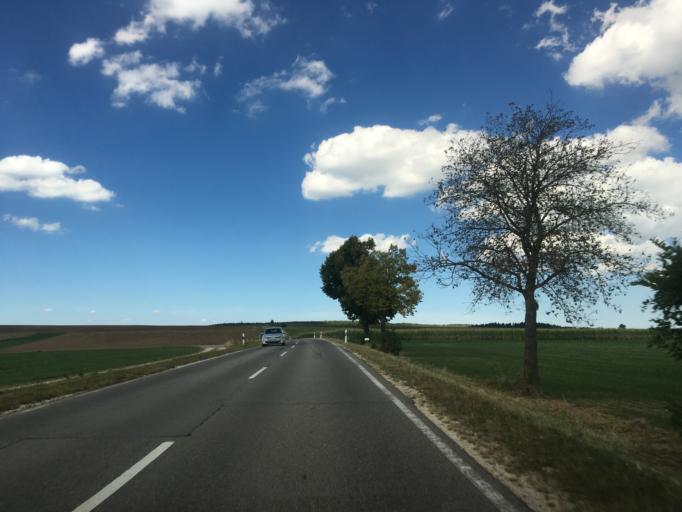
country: DE
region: Baden-Wuerttemberg
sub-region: Tuebingen Region
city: Hayingen
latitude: 48.3098
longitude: 9.4455
